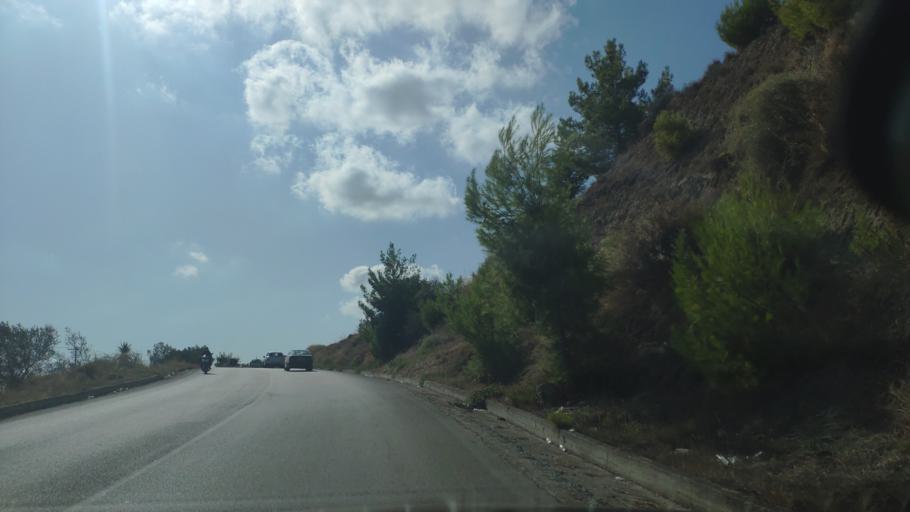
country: GR
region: Peloponnese
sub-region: Nomos Korinthias
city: Moulki
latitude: 37.9984
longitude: 22.7178
